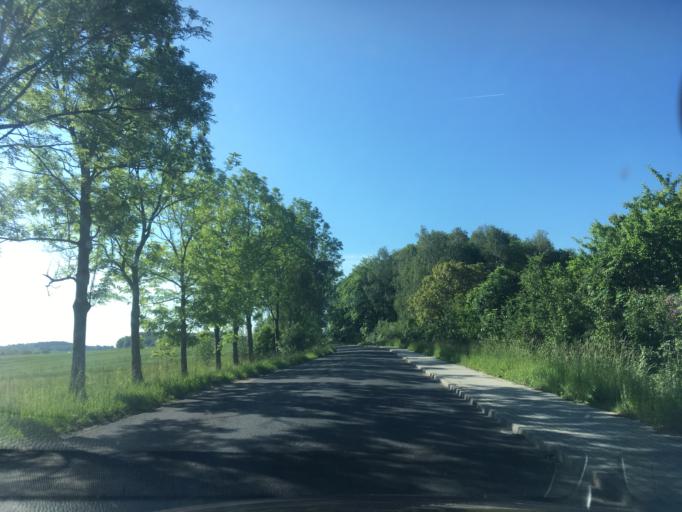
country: PL
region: Lower Silesian Voivodeship
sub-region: Powiat zgorzelecki
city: Zgorzelec
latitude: 51.1249
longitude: 15.0187
